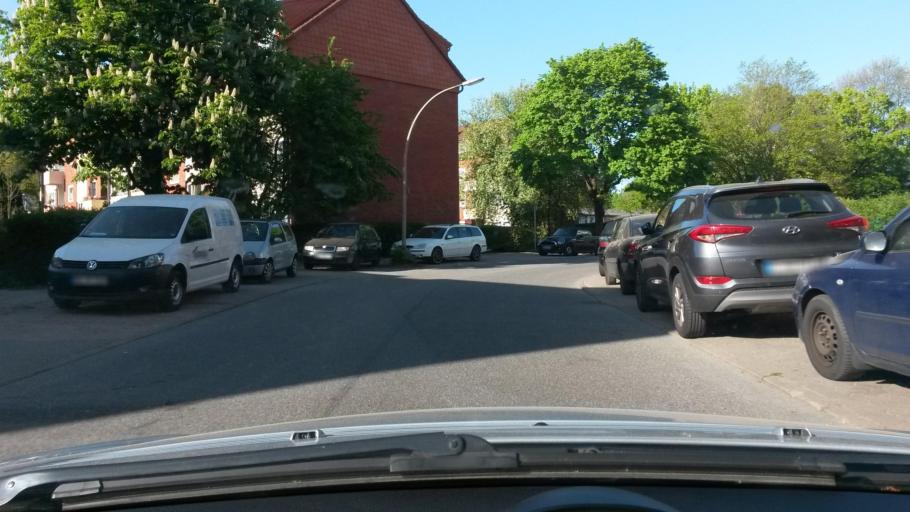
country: DE
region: Hamburg
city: Farmsen-Berne
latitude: 53.6224
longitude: 10.1317
